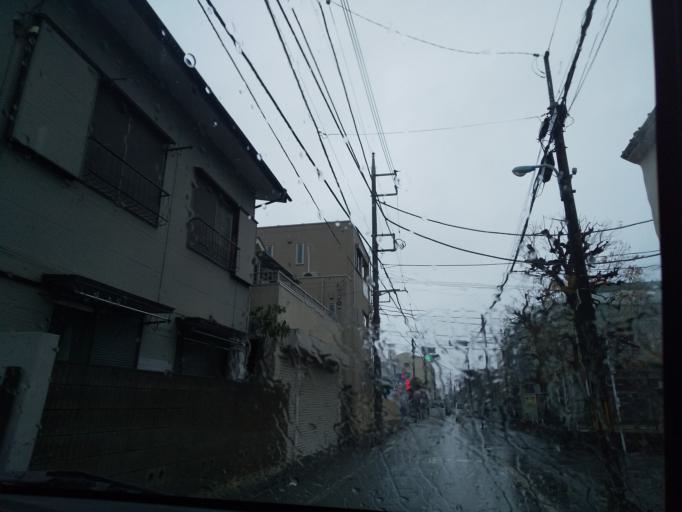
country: JP
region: Tokyo
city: Hino
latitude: 35.6919
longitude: 139.4159
